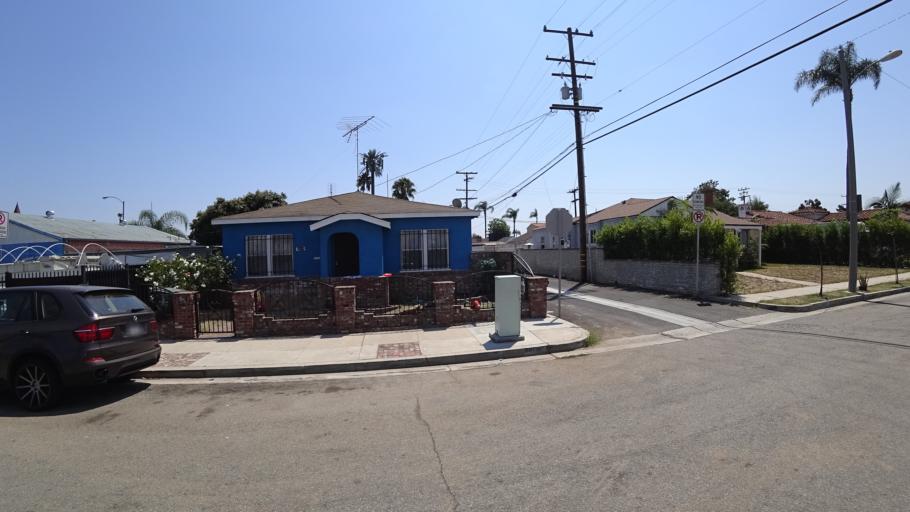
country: US
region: California
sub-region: Los Angeles County
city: Westmont
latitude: 33.9596
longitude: -118.3199
